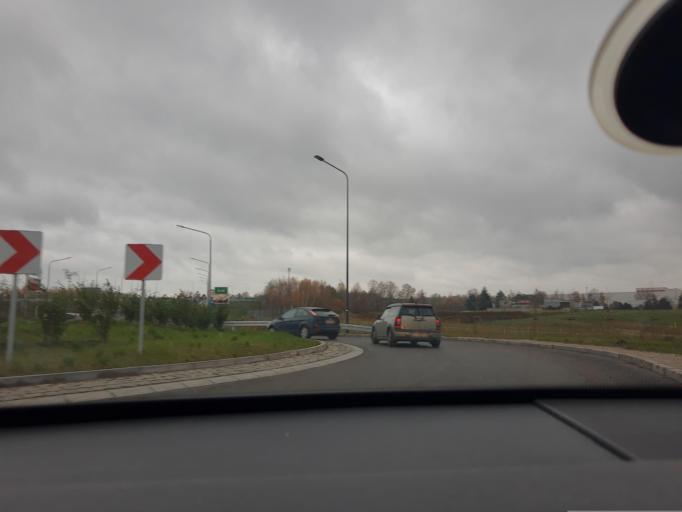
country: PL
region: Lodz Voivodeship
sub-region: Powiat pabianicki
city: Konstantynow Lodzki
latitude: 51.7307
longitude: 19.3589
